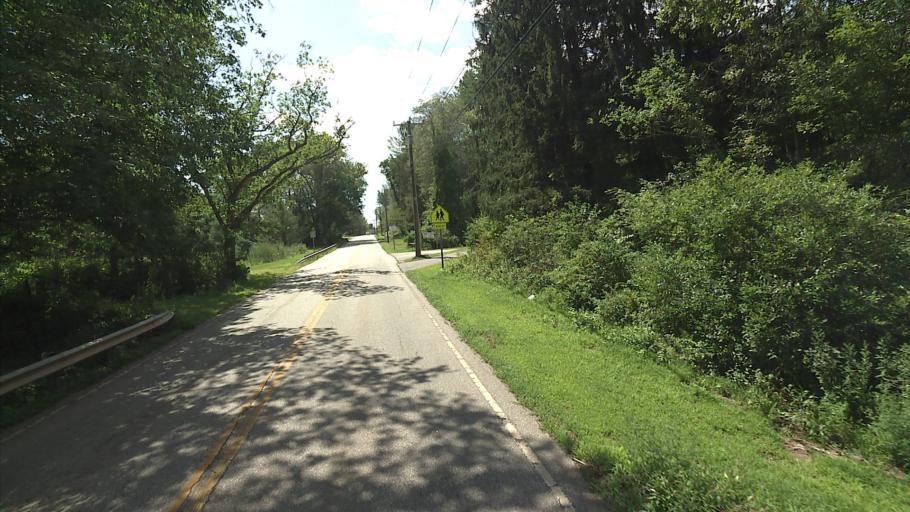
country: US
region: Connecticut
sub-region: Windham County
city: Windham
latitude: 41.7431
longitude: -72.1571
